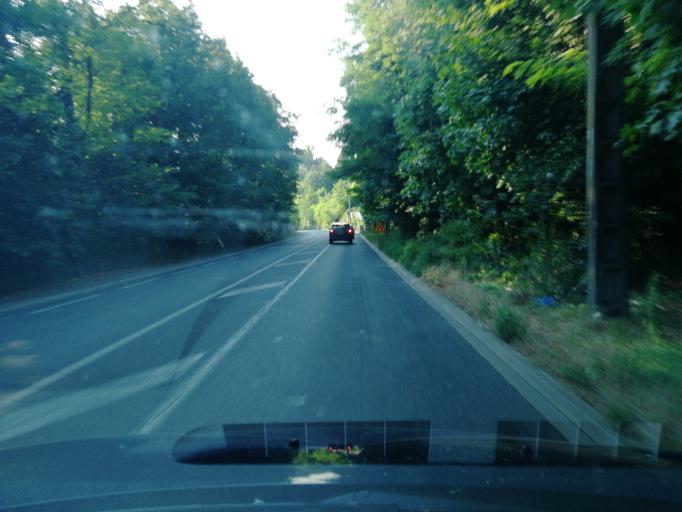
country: FR
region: Rhone-Alpes
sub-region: Departement du Rhone
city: Sathonay-Camp
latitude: 45.8270
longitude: 4.8599
